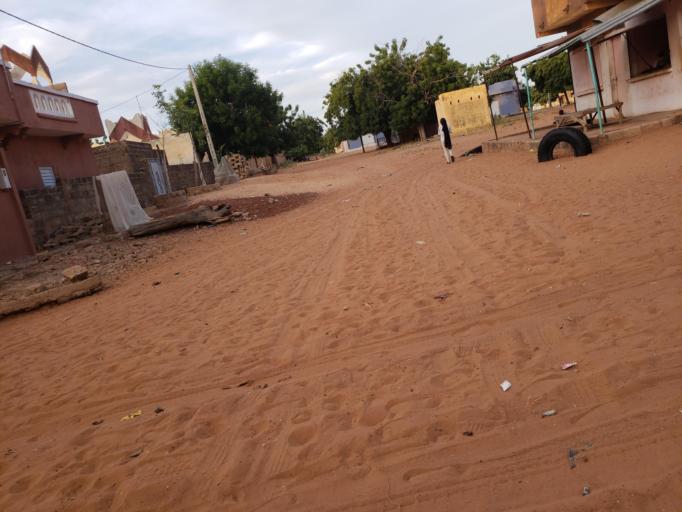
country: SN
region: Louga
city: Ndibene Dahra
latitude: 15.3969
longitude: -15.1123
